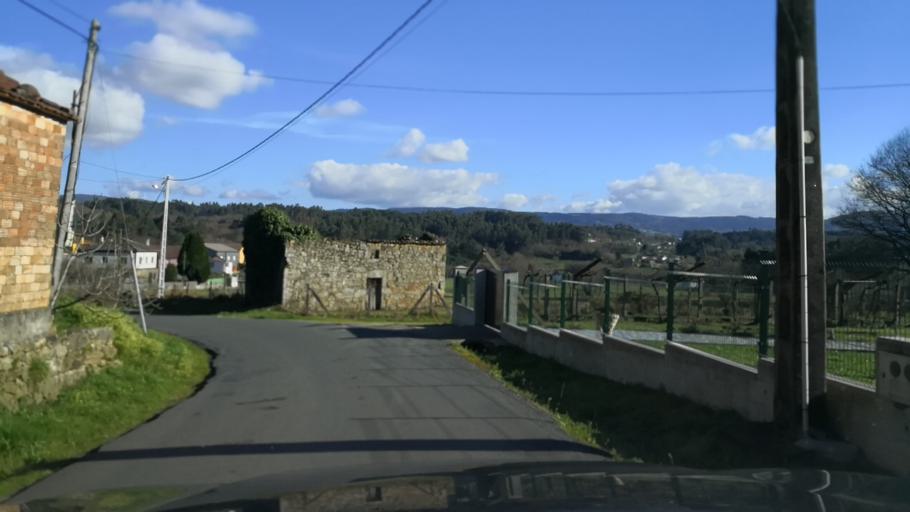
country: ES
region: Galicia
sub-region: Provincia da Coruna
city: Ribeira
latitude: 42.7161
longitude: -8.4389
